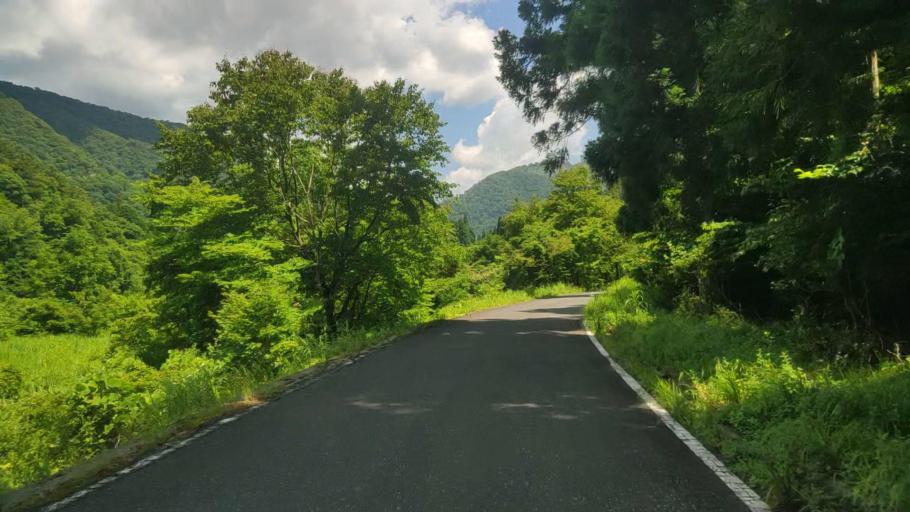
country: JP
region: Fukui
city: Ono
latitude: 35.7557
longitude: 136.5734
